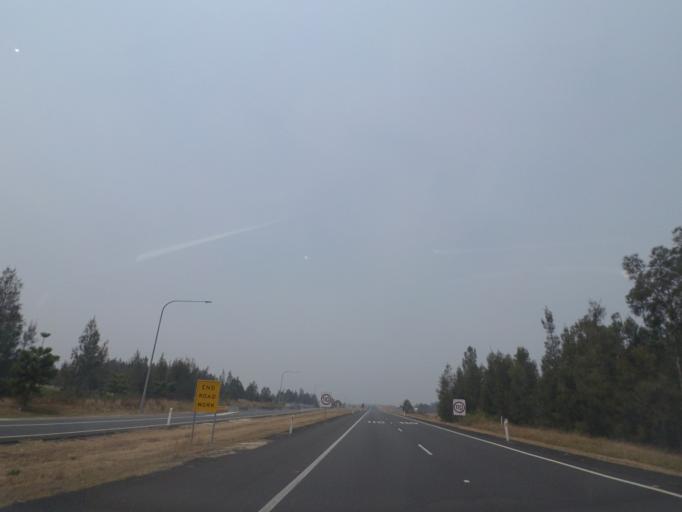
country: AU
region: New South Wales
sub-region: Ballina
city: Ballina
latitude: -28.8633
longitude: 153.5129
